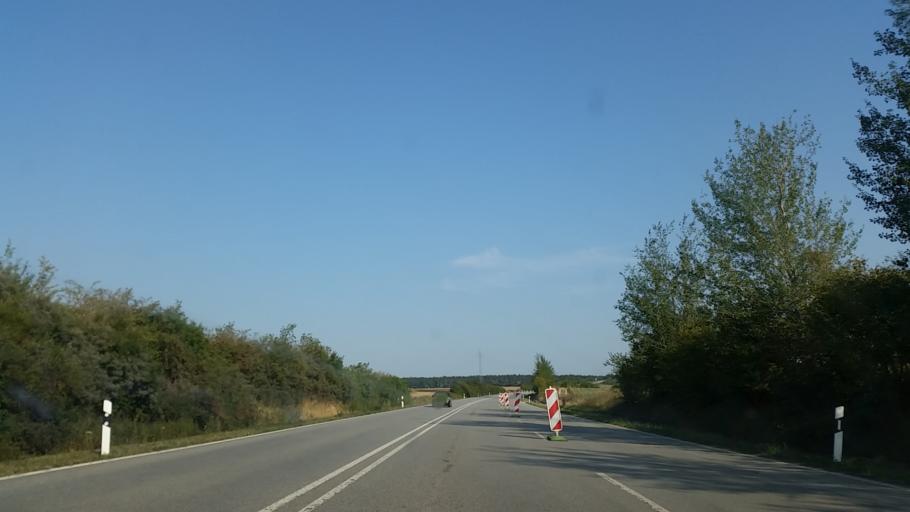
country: DE
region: Brandenburg
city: Pinnow
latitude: 53.0735
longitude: 14.1023
